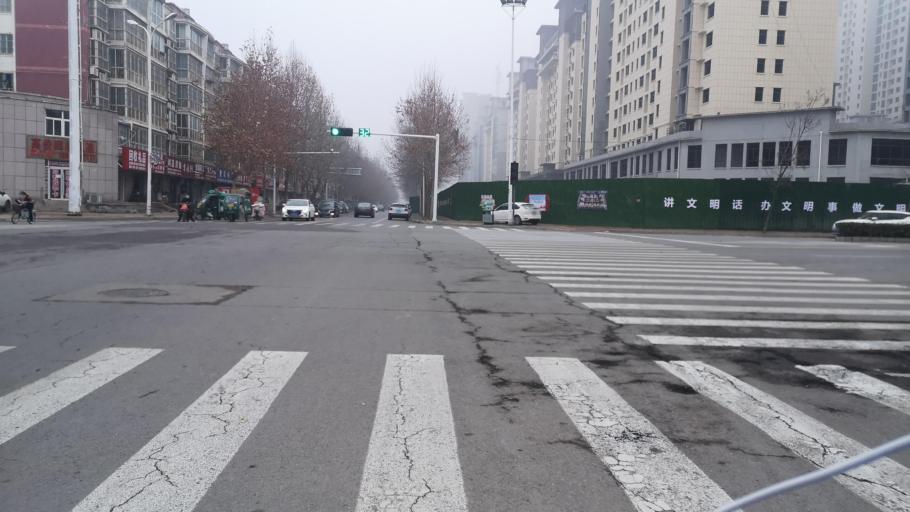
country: CN
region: Henan Sheng
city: Zhongyuanlu
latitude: 35.7641
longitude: 115.0787
